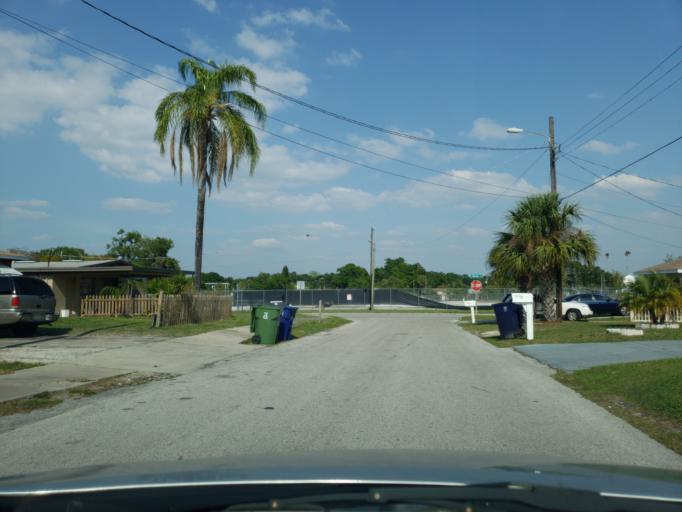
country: US
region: Florida
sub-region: Hillsborough County
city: Tampa
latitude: 27.9645
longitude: -82.4771
